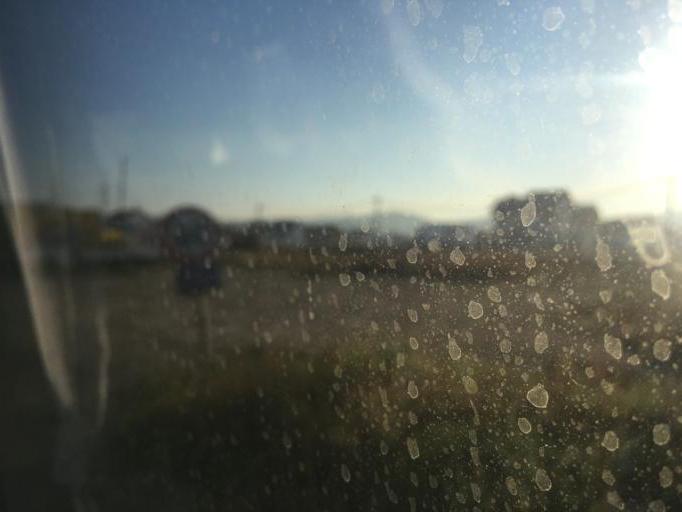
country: XK
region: Pristina
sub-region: Komuna e Drenasit
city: Glogovac
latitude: 42.6257
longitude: 20.8989
